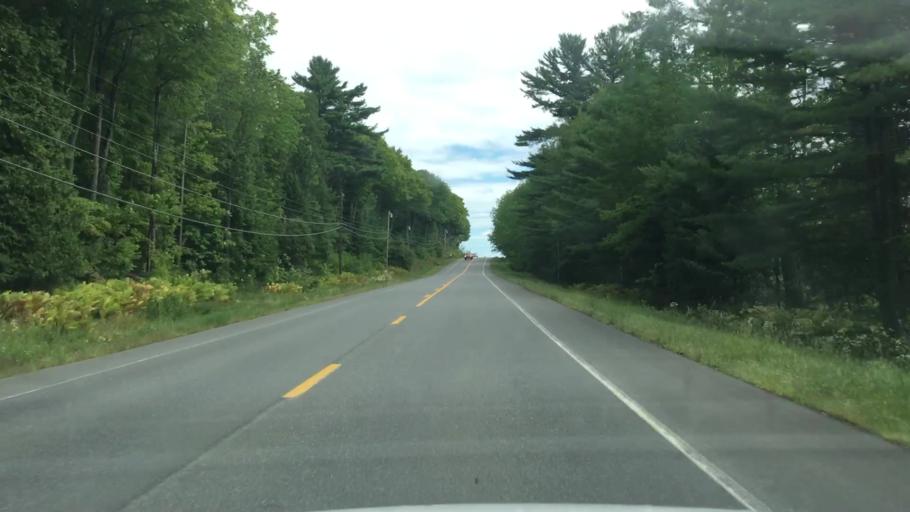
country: US
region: Maine
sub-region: Piscataquis County
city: Dover-Foxcroft
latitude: 45.2238
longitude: -69.1288
